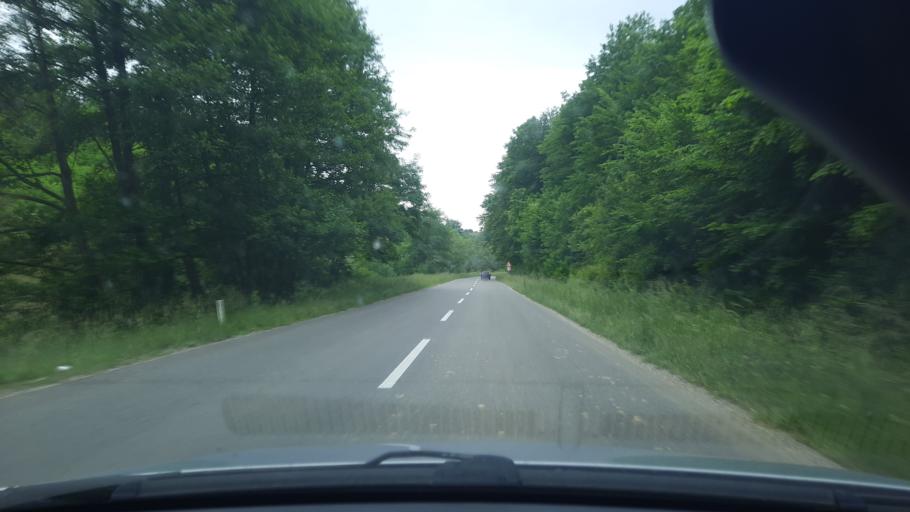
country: RS
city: Bukor
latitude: 44.5070
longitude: 19.4978
